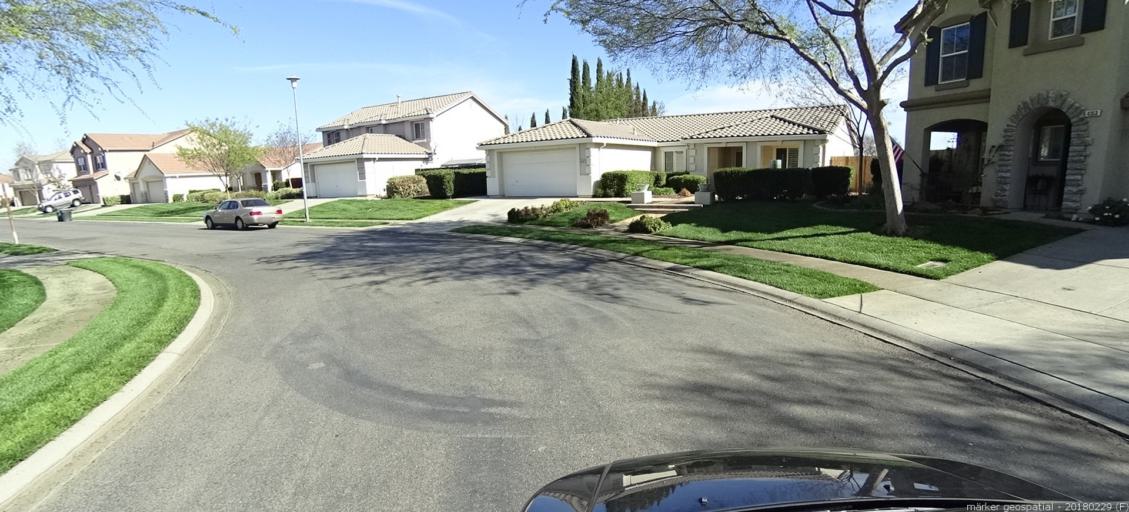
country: US
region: California
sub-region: Sacramento County
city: Rancho Cordova
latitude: 38.5460
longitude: -121.2744
